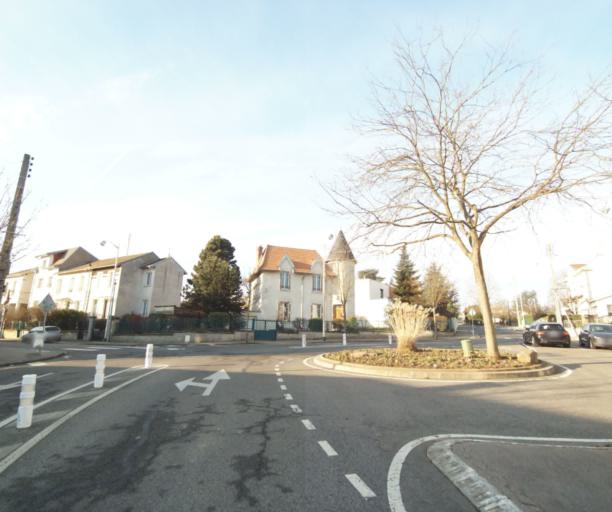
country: FR
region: Lorraine
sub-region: Departement de Meurthe-et-Moselle
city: Laxou
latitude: 48.6947
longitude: 6.1479
